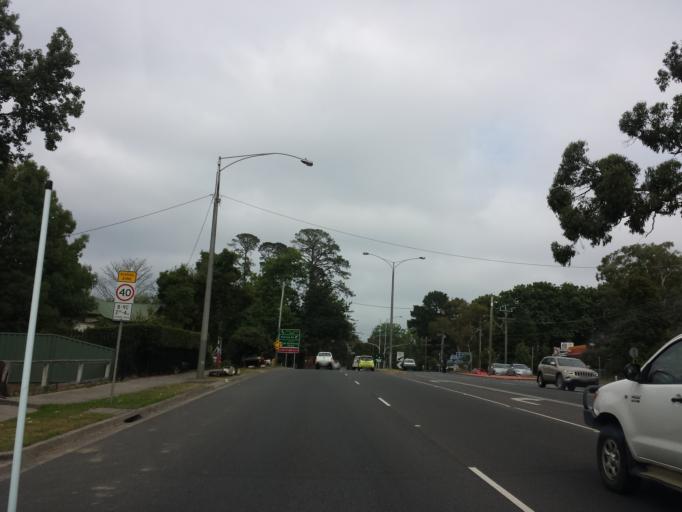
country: AU
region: Victoria
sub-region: Yarra Ranges
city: Montrose
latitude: -37.8091
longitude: 145.3448
